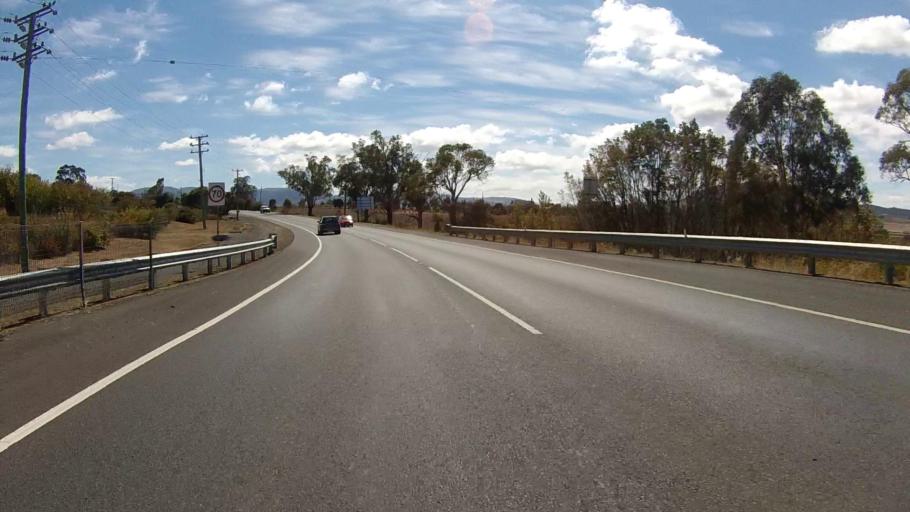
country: AU
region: Tasmania
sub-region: Brighton
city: Bridgewater
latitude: -42.7123
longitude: 147.2440
